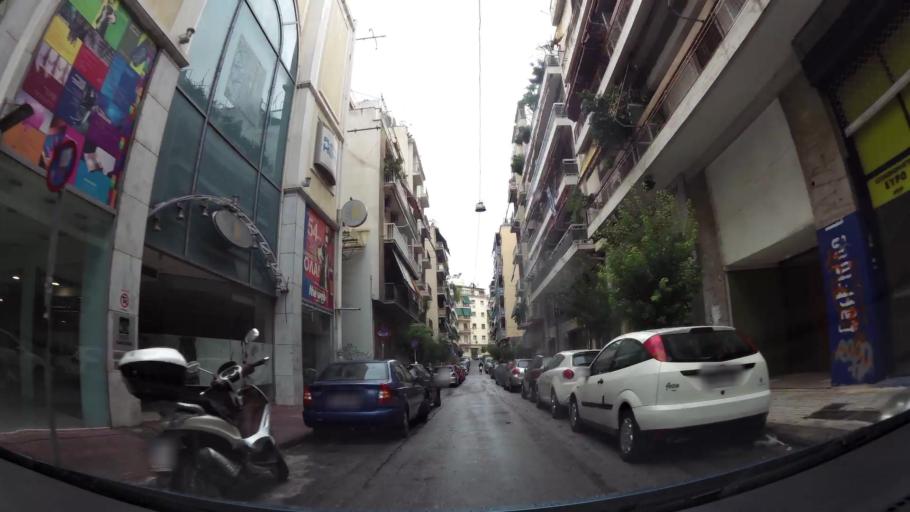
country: GR
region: Attica
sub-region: Nomarchia Athinas
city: Vyronas
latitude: 37.9674
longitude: 23.7481
